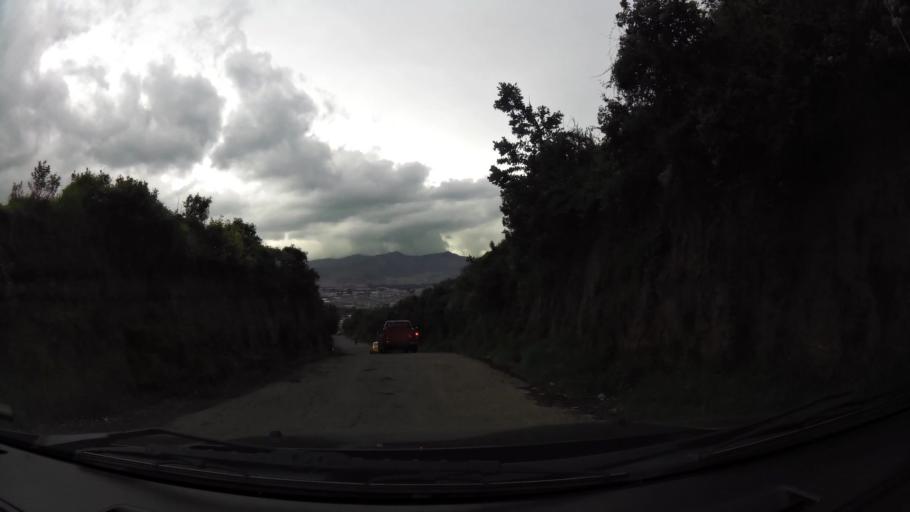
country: EC
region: Pichincha
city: Sangolqui
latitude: -0.3187
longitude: -78.5314
